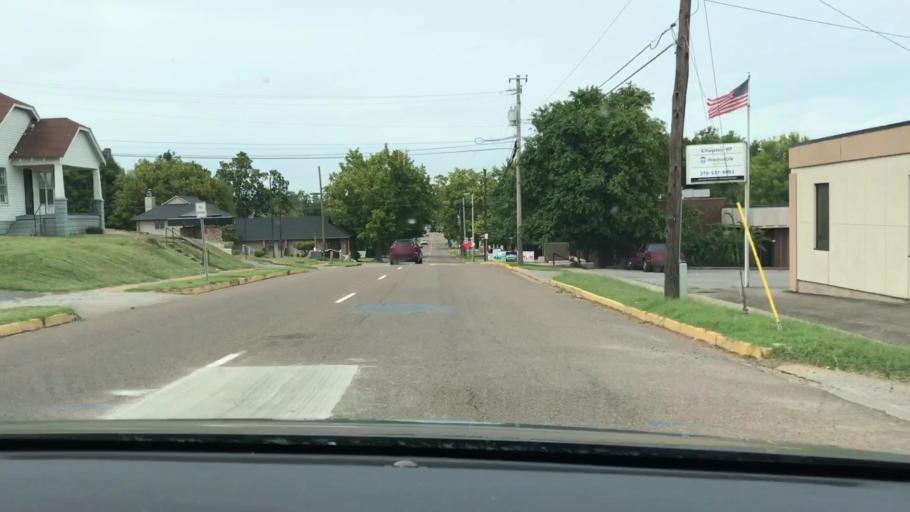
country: US
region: Kentucky
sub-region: Marshall County
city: Benton
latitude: 36.8583
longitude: -88.3499
